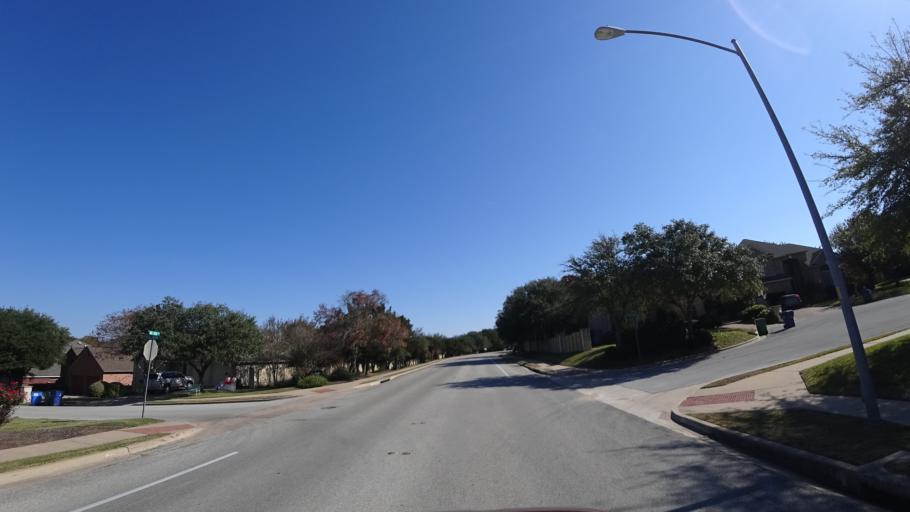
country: US
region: Texas
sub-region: Travis County
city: Lost Creek
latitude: 30.3764
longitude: -97.8485
